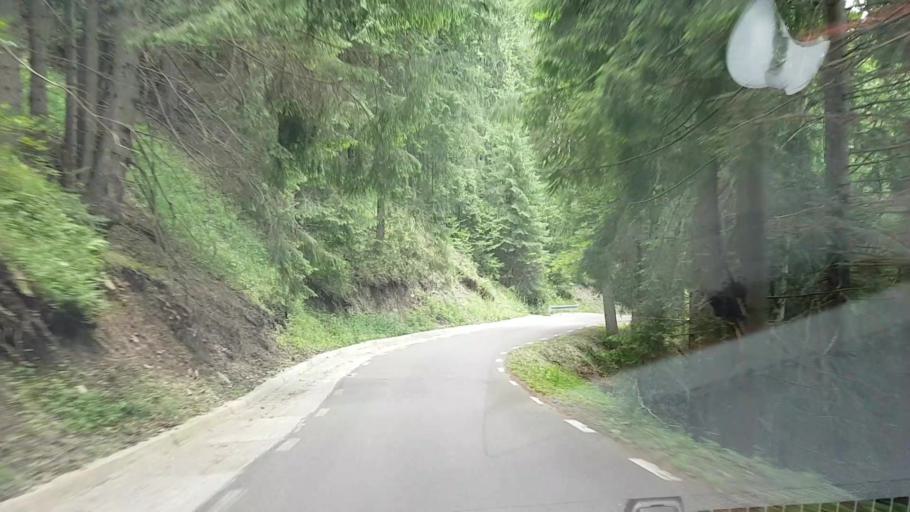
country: RO
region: Suceava
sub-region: Municipiul Campulung Moldovenesc
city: Campulung Moldovenesc
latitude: 47.4365
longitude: 25.5668
